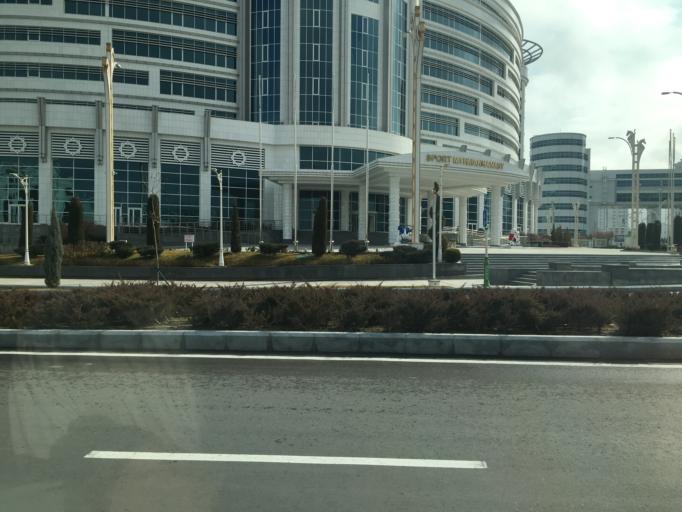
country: TM
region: Ahal
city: Ashgabat
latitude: 37.8975
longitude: 58.3704
